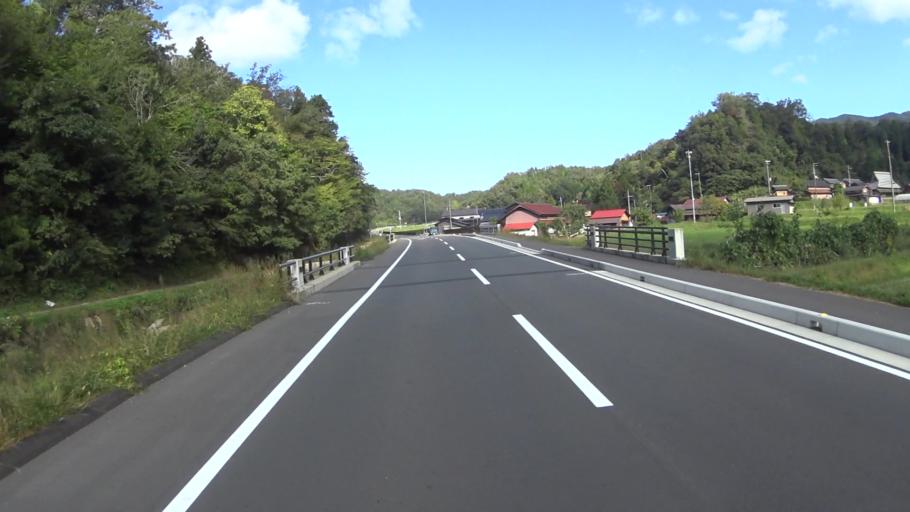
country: JP
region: Kyoto
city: Miyazu
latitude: 35.6099
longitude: 135.1347
